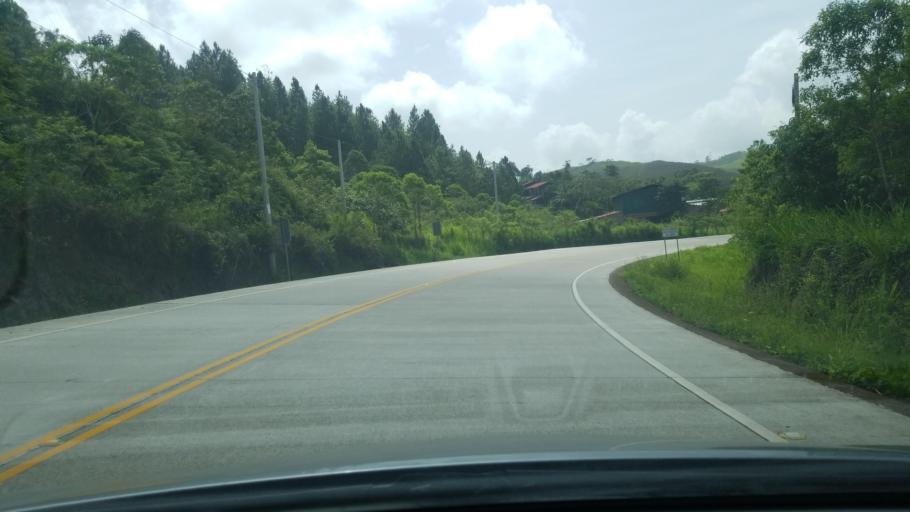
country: HN
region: Copan
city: San Jeronimo
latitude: 14.9352
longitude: -88.9292
